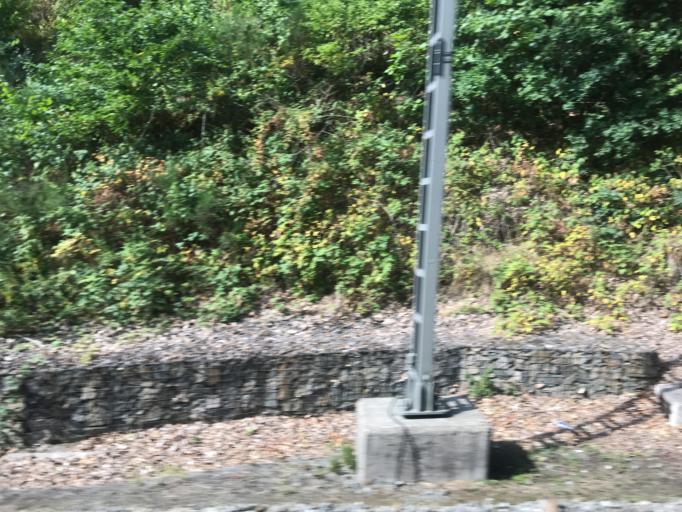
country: CZ
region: Central Bohemia
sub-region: Okres Benesov
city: Cercany
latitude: 49.8283
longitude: 14.7022
